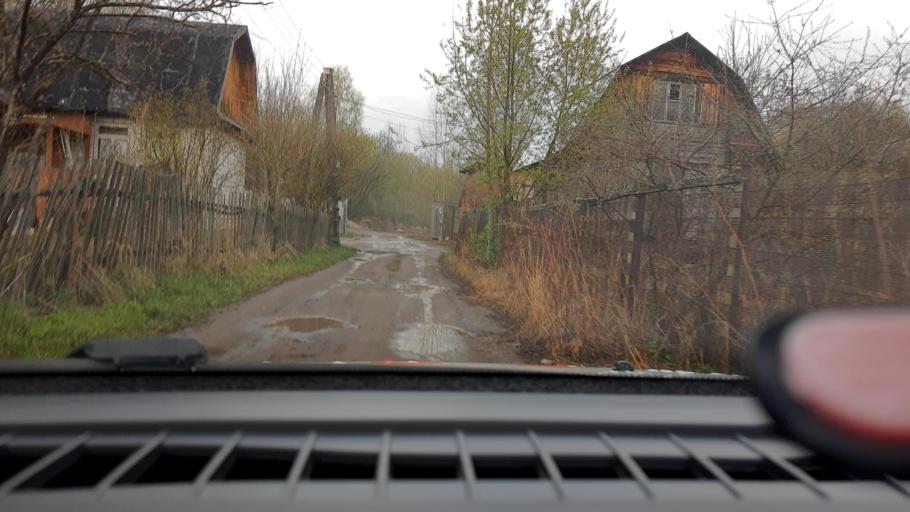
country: RU
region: Nizjnij Novgorod
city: Gorbatovka
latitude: 56.2987
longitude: 43.7694
